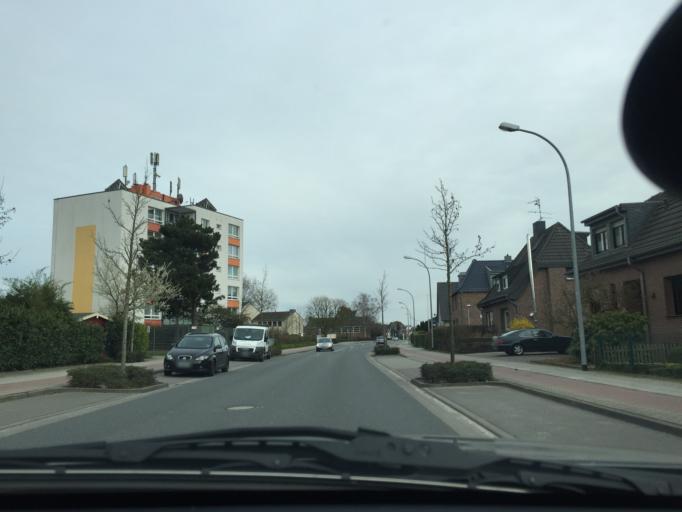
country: DE
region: North Rhine-Westphalia
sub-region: Regierungsbezirk Dusseldorf
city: Goch
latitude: 51.6770
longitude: 6.1481
